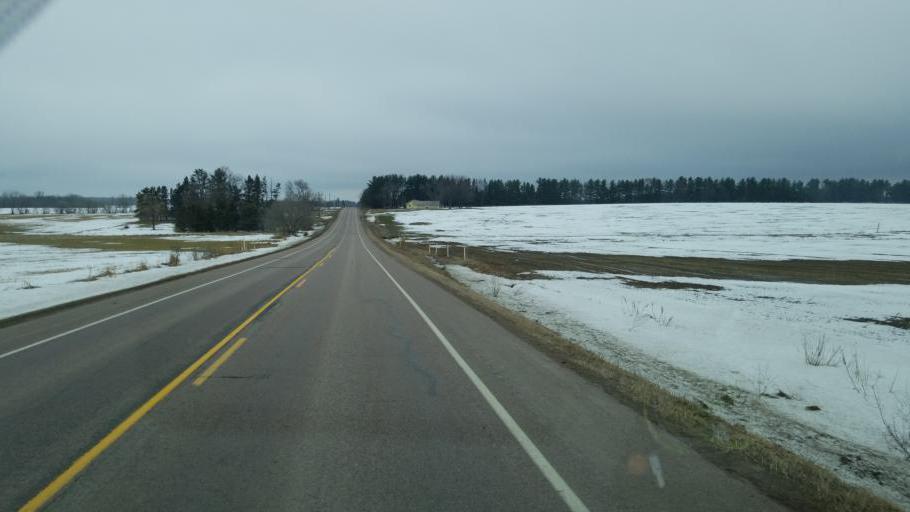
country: US
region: Wisconsin
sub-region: Wood County
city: Marshfield
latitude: 44.6449
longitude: -90.2184
